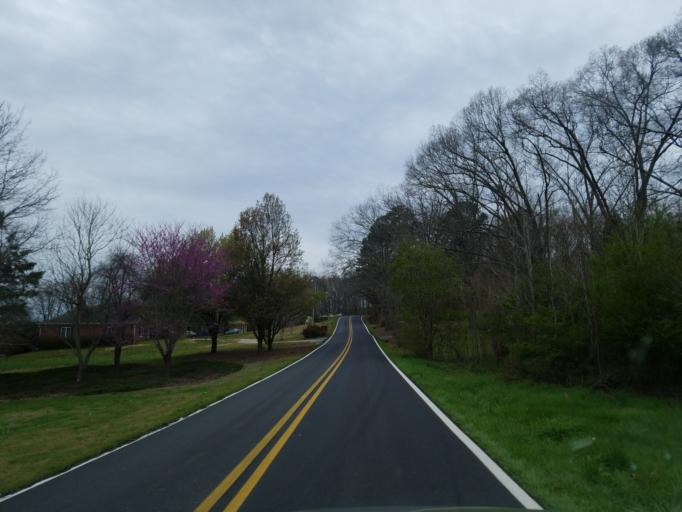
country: US
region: Georgia
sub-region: Bartow County
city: Cartersville
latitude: 34.2186
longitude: -84.7806
